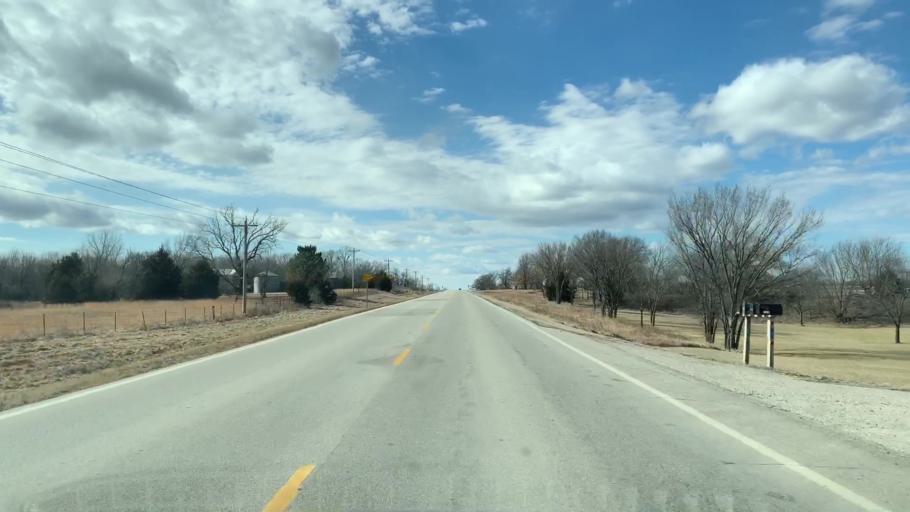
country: US
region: Kansas
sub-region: Neosho County
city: Erie
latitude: 37.5292
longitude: -95.2750
